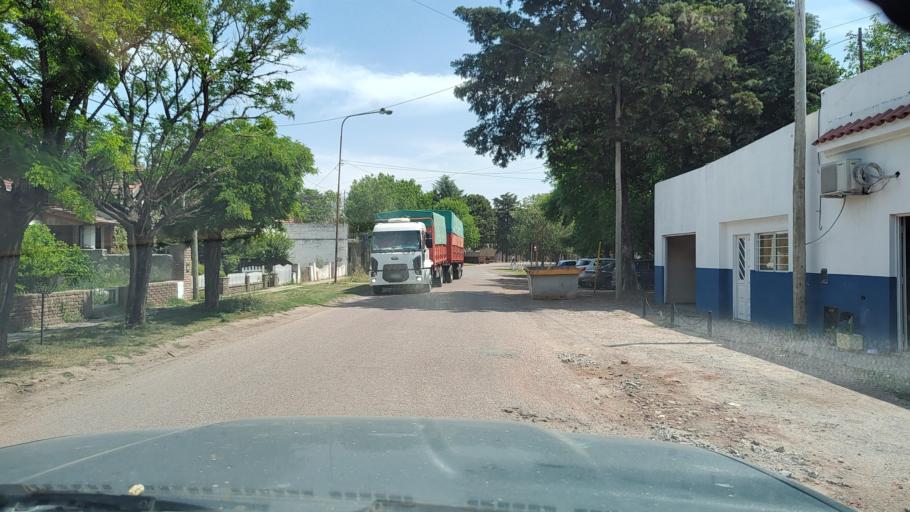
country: AR
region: Buenos Aires
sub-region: Partido de Lujan
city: Lujan
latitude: -34.6010
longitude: -59.1763
